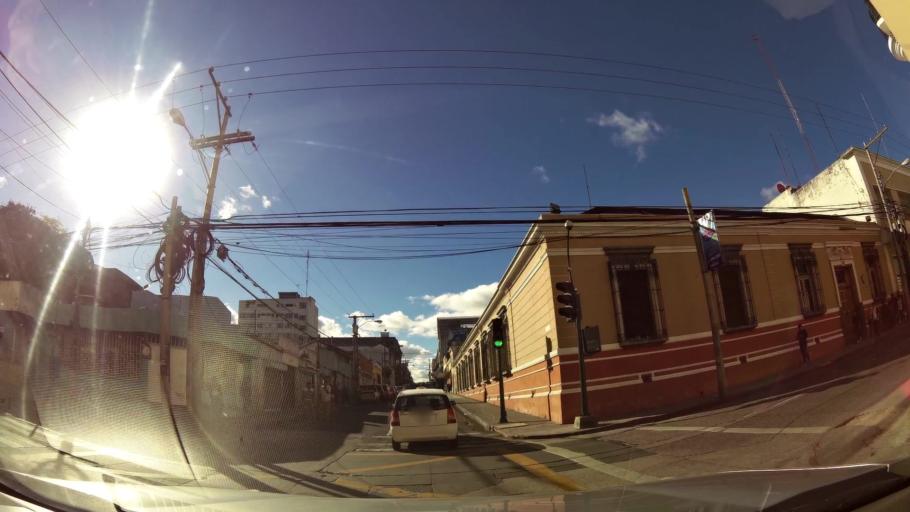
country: GT
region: Guatemala
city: Guatemala City
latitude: 14.6371
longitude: -90.5131
